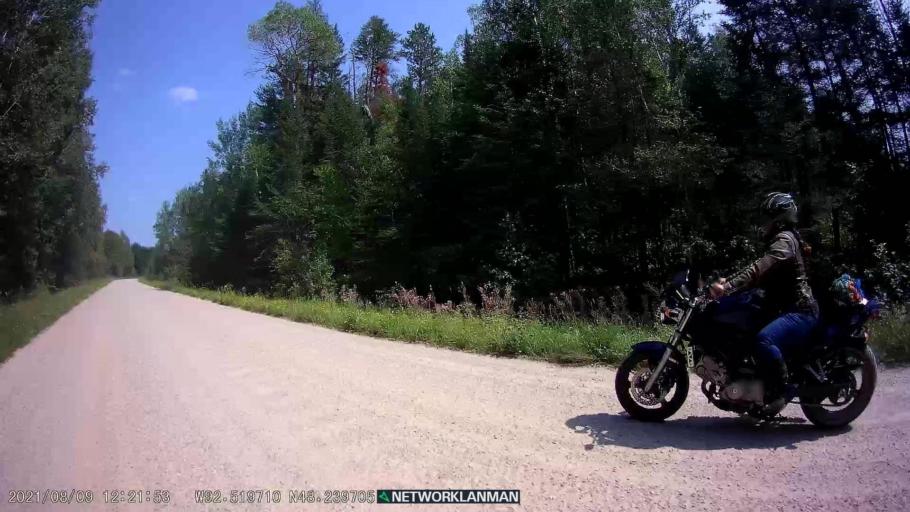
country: US
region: Minnesota
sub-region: Saint Louis County
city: Parkville
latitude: 48.2398
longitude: -92.5195
